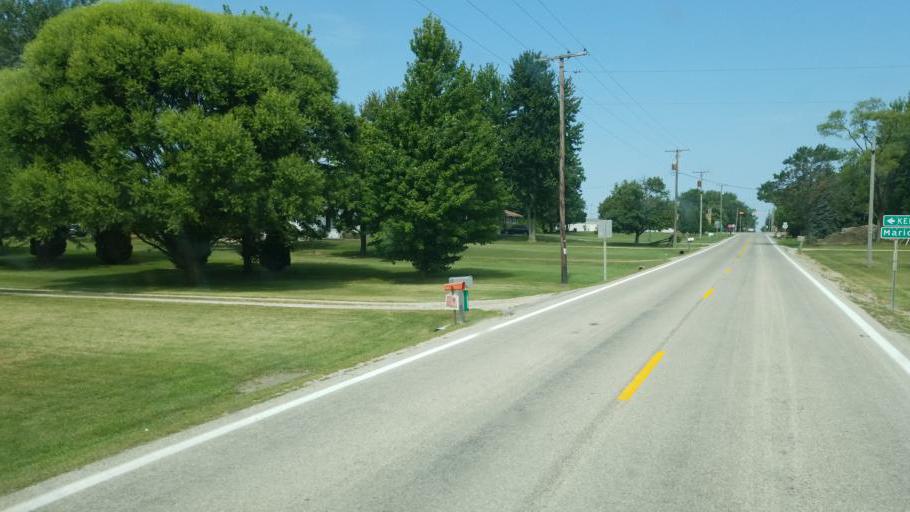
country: US
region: Ohio
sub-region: Marion County
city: Marion
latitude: 40.6105
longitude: -83.2173
